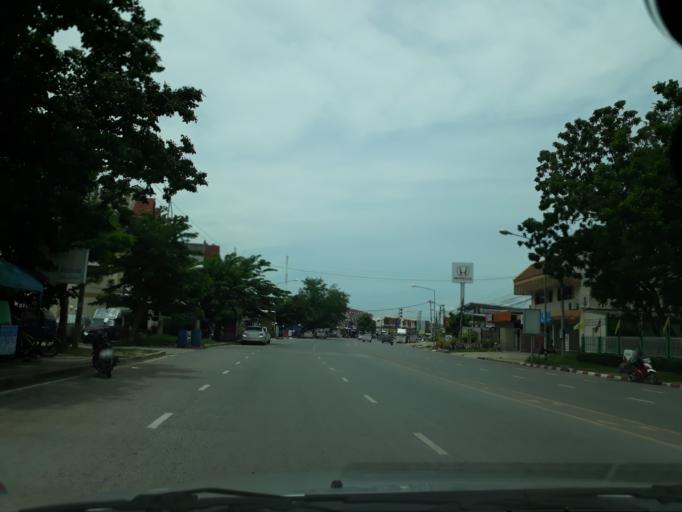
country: TH
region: Khon Kaen
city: Khon Kaen
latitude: 16.4329
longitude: 102.8671
